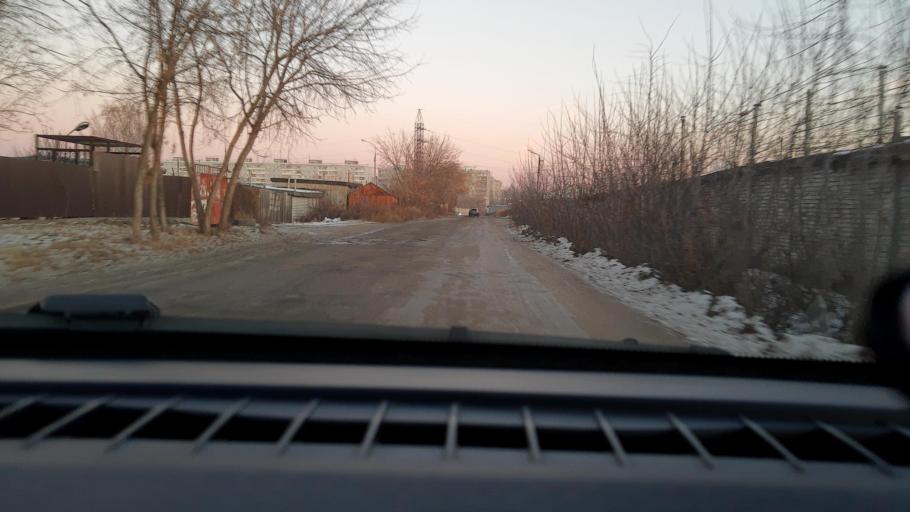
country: RU
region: Nizjnij Novgorod
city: Gorbatovka
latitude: 56.2547
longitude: 43.8361
